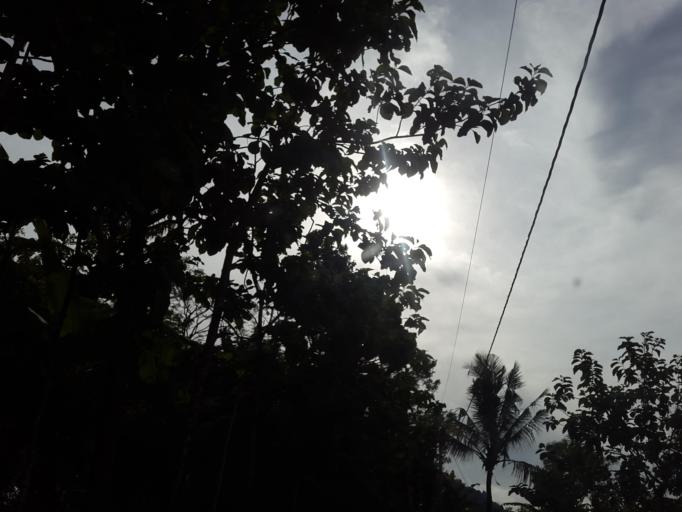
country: ID
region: Central Java
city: Trucuk
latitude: -7.8204
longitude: 110.6644
